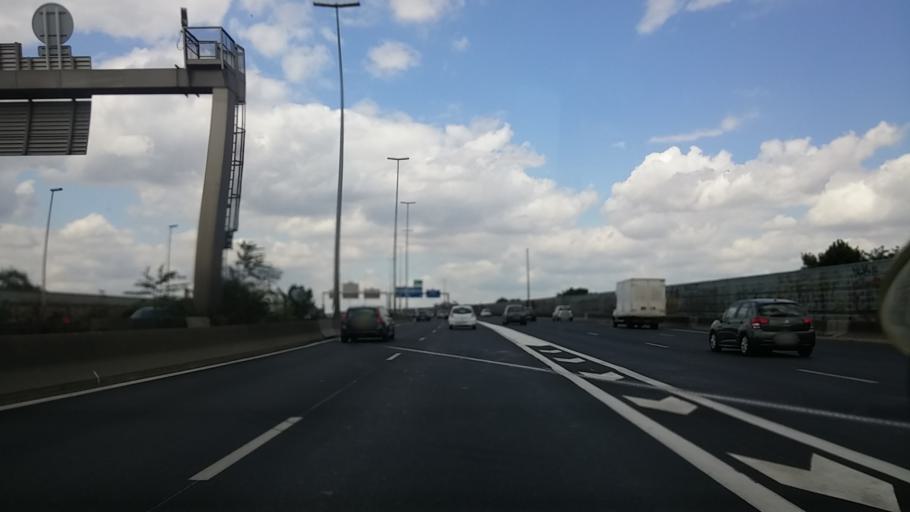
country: FR
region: Ile-de-France
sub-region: Departement de Seine-Saint-Denis
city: Noisy-le-Sec
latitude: 48.8905
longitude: 2.4735
